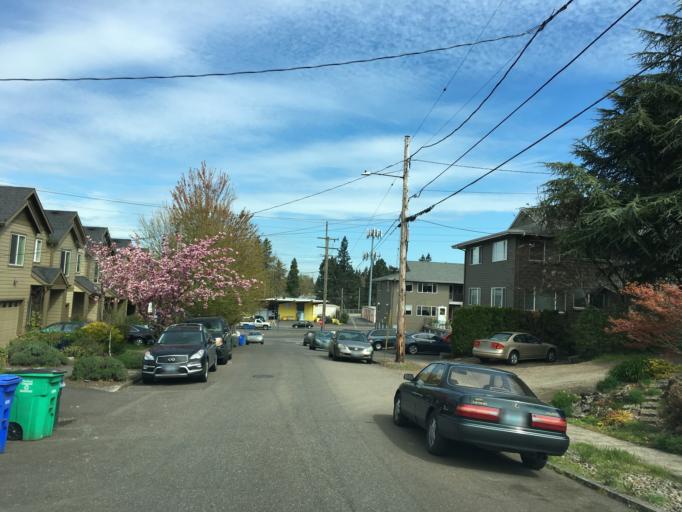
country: US
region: Oregon
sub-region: Multnomah County
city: Lents
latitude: 45.5326
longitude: -122.5919
